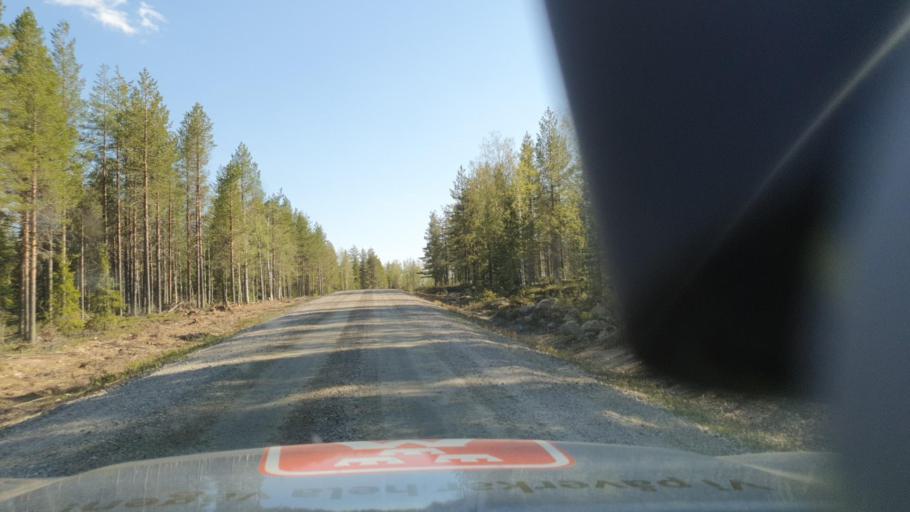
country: SE
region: Norrbotten
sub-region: Bodens Kommun
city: Boden
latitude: 66.4569
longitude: 21.8668
